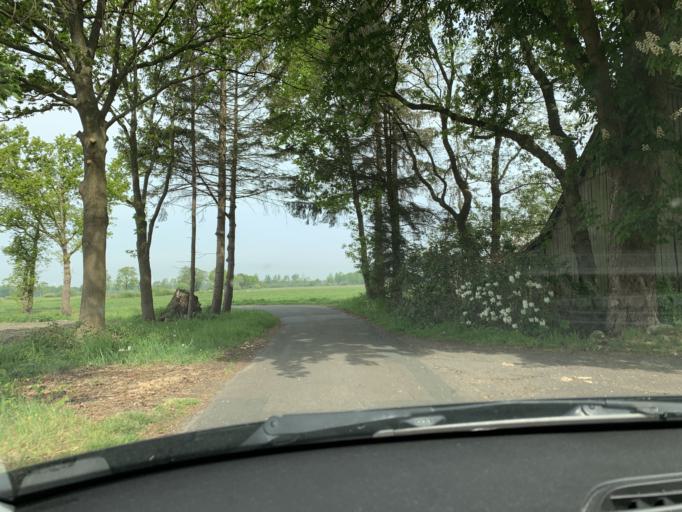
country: DE
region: Lower Saxony
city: Apen
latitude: 53.2376
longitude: 7.8339
